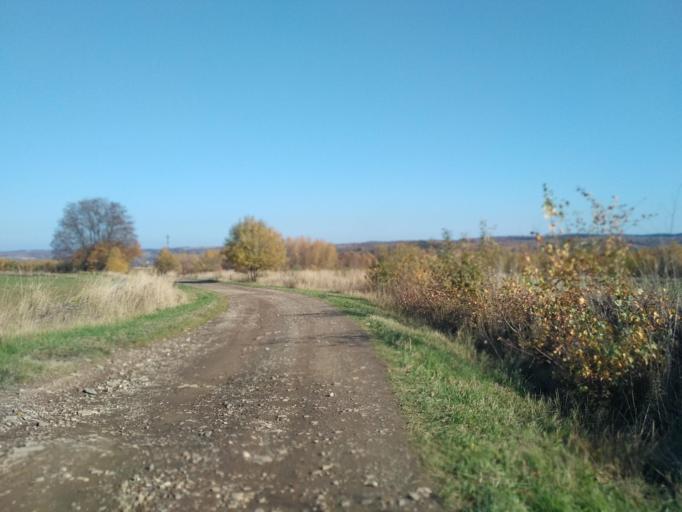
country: PL
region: Subcarpathian Voivodeship
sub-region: Powiat rzeszowski
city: Blazowa
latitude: 49.8681
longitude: 22.0862
